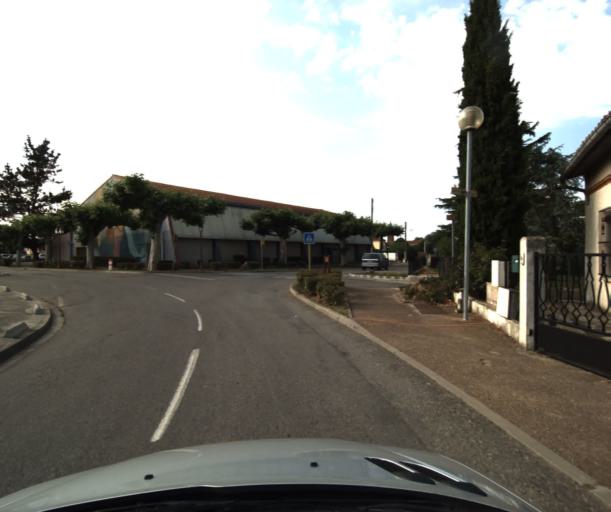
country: FR
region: Midi-Pyrenees
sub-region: Departement de la Haute-Garonne
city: Fonsorbes
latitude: 43.5328
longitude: 1.2314
